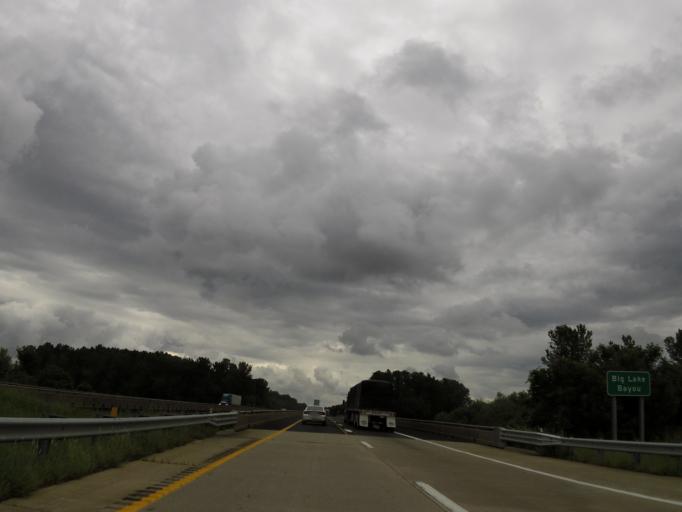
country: US
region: Illinois
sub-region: Alexander County
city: Cairo
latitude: 37.0067
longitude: -89.2240
